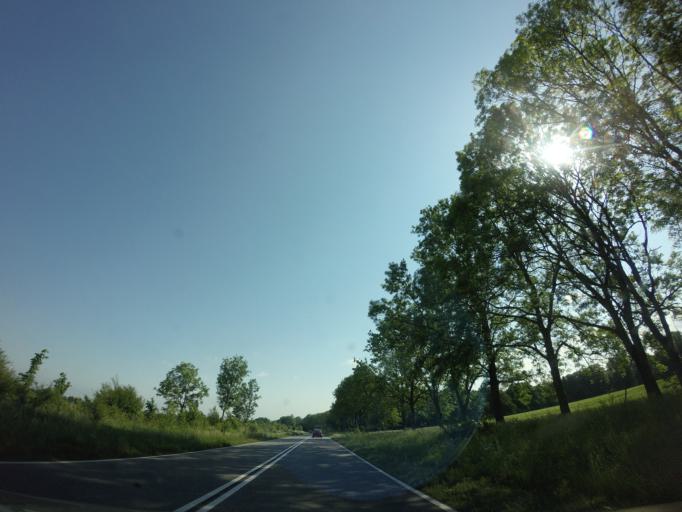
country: PL
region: West Pomeranian Voivodeship
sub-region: Powiat gryfinski
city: Stare Czarnowo
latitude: 53.3097
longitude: 14.7929
